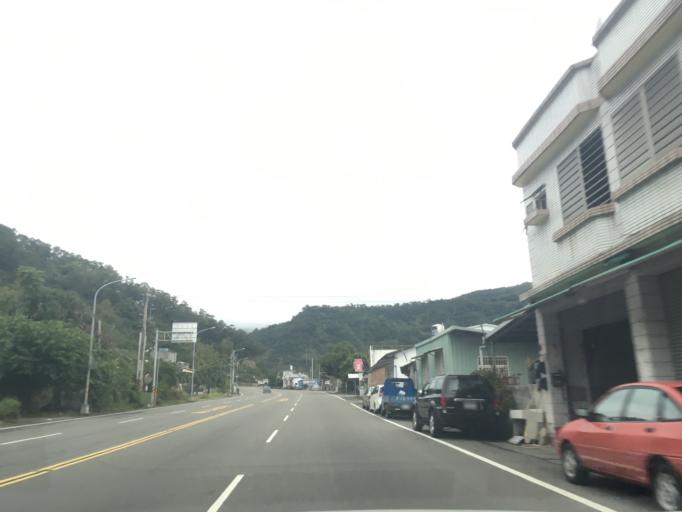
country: TW
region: Taiwan
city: Taitung City
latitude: 22.7575
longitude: 121.0520
